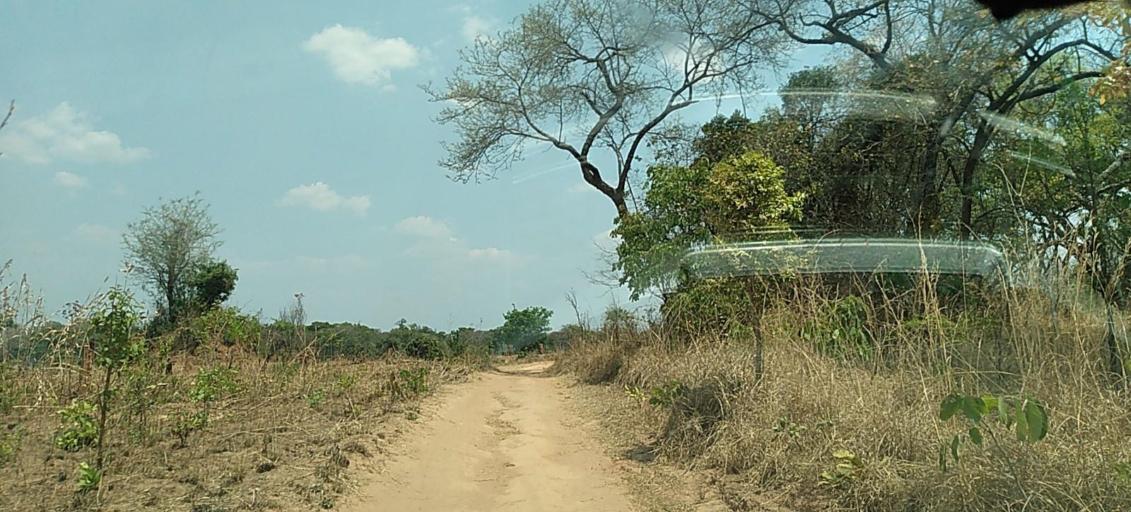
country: ZM
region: North-Western
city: Kasempa
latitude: -13.5312
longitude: 25.8226
